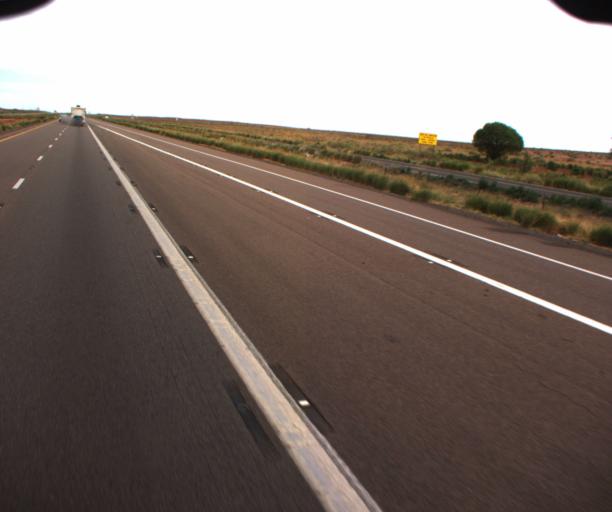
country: US
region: Arizona
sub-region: Coconino County
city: LeChee
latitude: 35.0687
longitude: -110.8393
